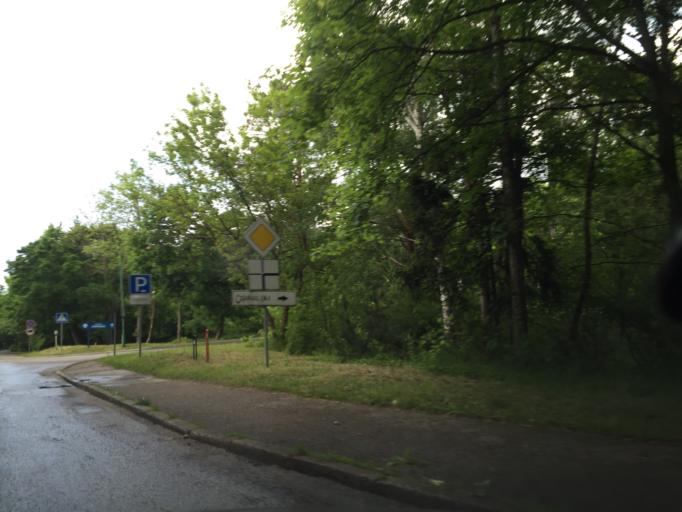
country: LT
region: Klaipedos apskritis
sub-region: Klaipeda
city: Klaipeda
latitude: 55.7656
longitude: 21.0872
